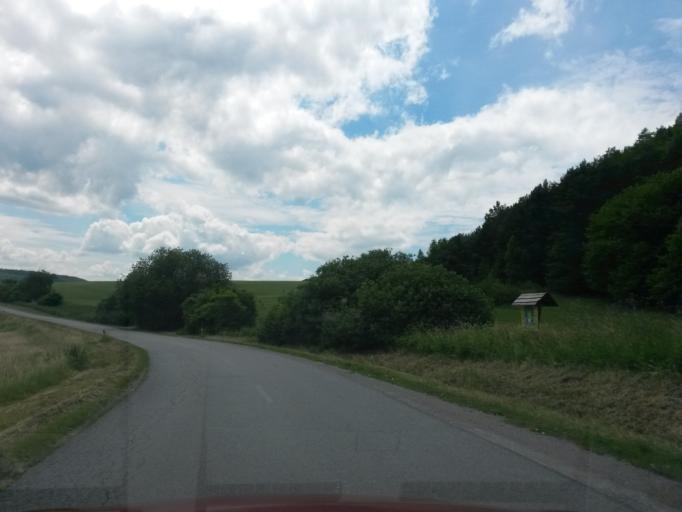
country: SK
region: Kosicky
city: Gelnica
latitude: 48.9348
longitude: 21.0455
